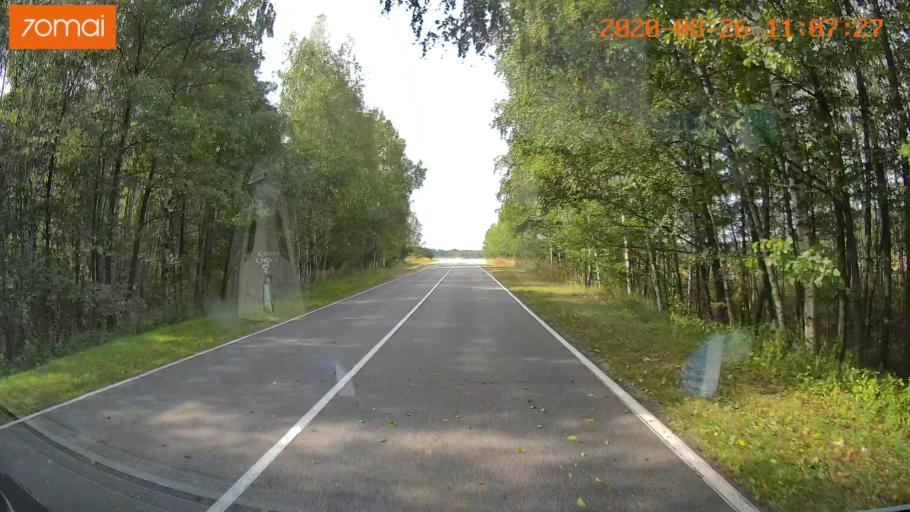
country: RU
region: Rjazan
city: Izhevskoye
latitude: 54.5180
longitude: 41.1244
